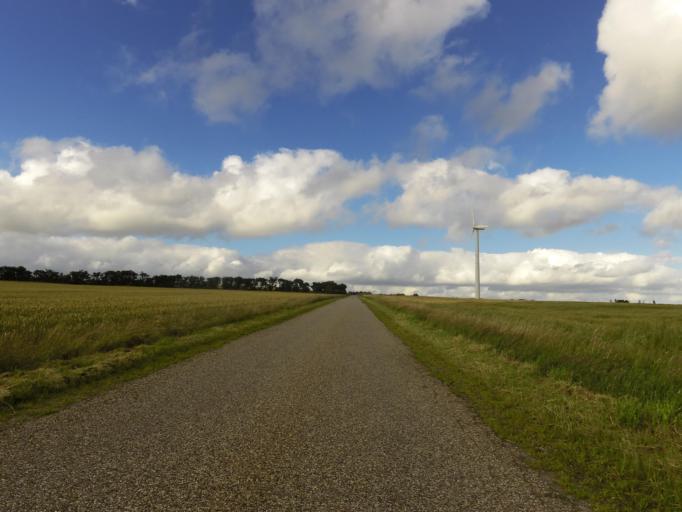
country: DK
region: South Denmark
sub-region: Tonder Kommune
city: Toftlund
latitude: 55.1402
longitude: 9.0794
